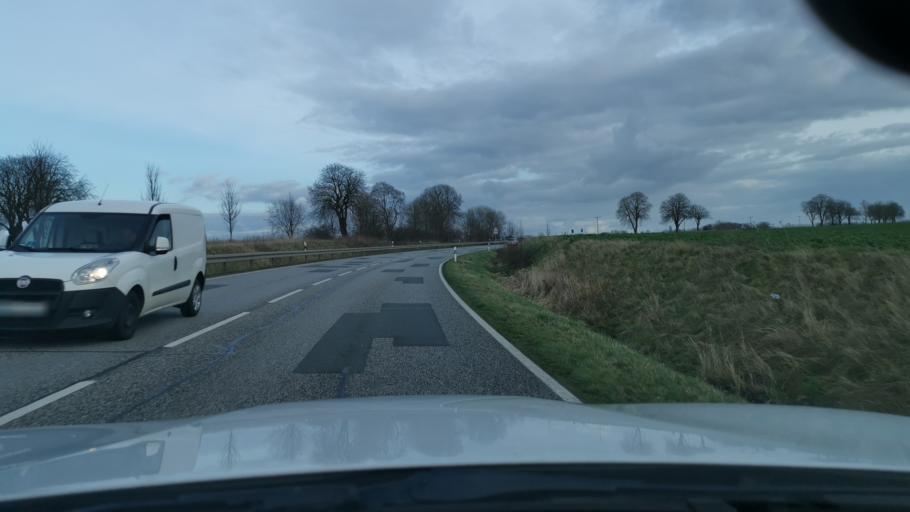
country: DE
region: Mecklenburg-Vorpommern
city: Dummerstorf
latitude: 54.0227
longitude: 12.2394
